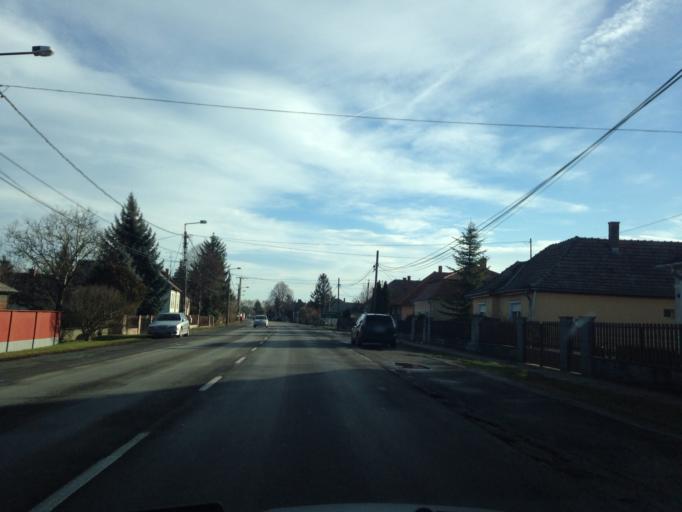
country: HU
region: Gyor-Moson-Sopron
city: Otteveny
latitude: 47.7302
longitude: 17.4834
